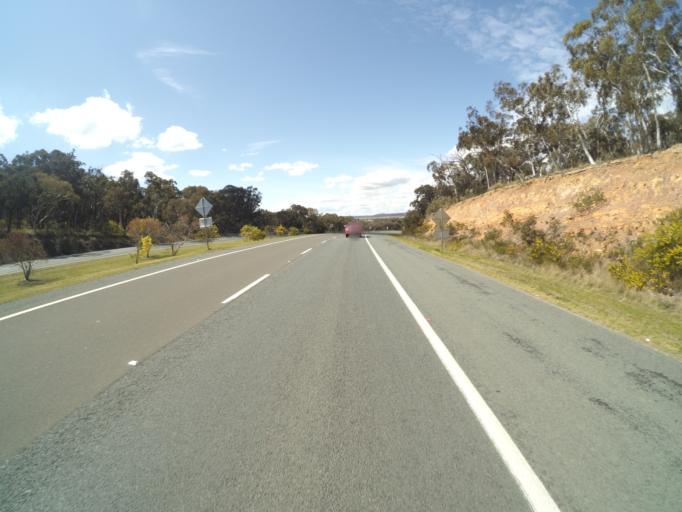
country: AU
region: New South Wales
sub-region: Goulburn Mulwaree
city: Goulburn
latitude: -34.7419
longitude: 149.7605
